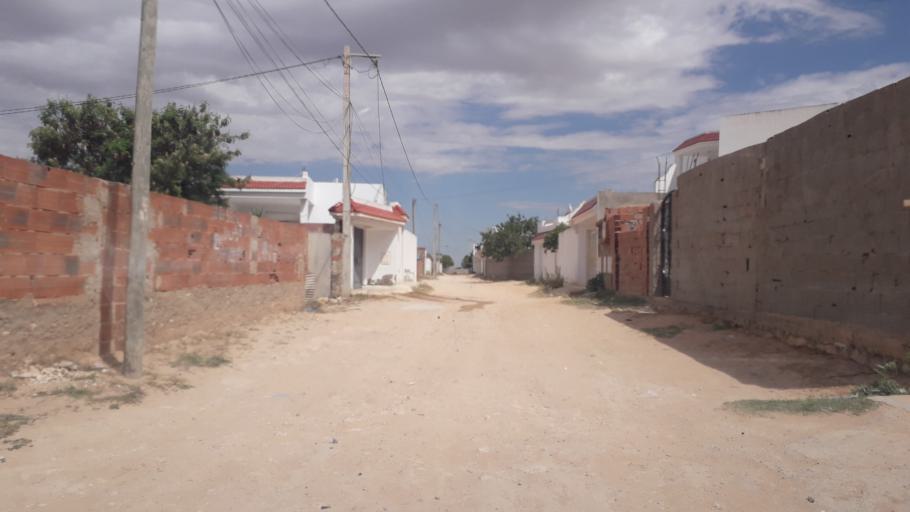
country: TN
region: Safaqis
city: Al Qarmadah
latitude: 34.8415
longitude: 10.7744
